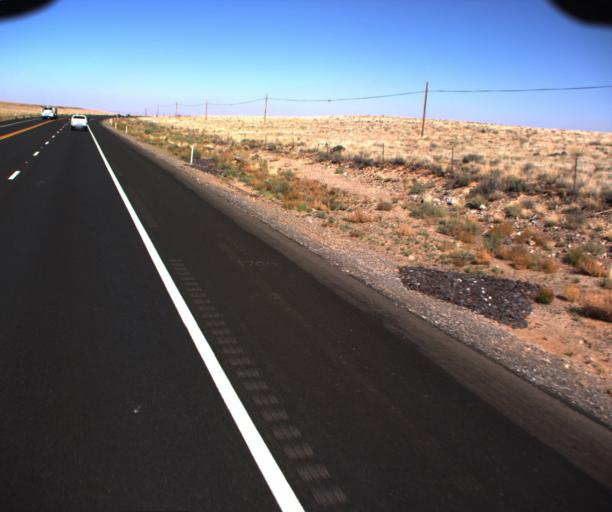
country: US
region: Arizona
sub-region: Coconino County
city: Flagstaff
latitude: 35.6883
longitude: -111.5051
